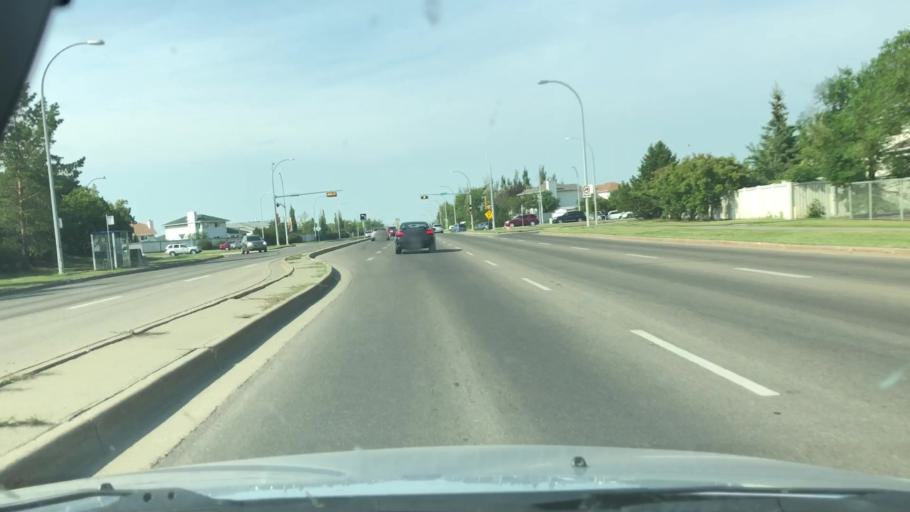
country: CA
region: Alberta
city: Edmonton
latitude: 53.6148
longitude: -113.4428
